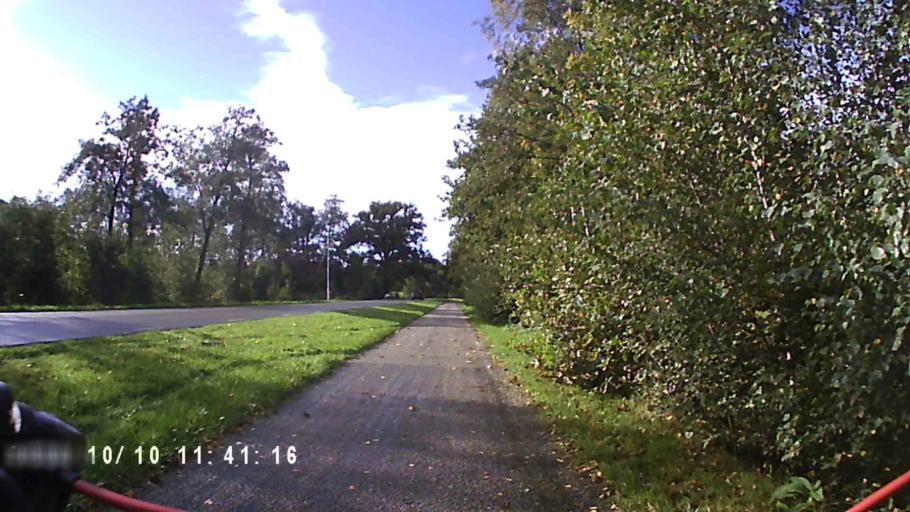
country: NL
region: Friesland
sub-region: Gemeente Smallingerland
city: Drachten
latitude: 53.0651
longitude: 6.1017
